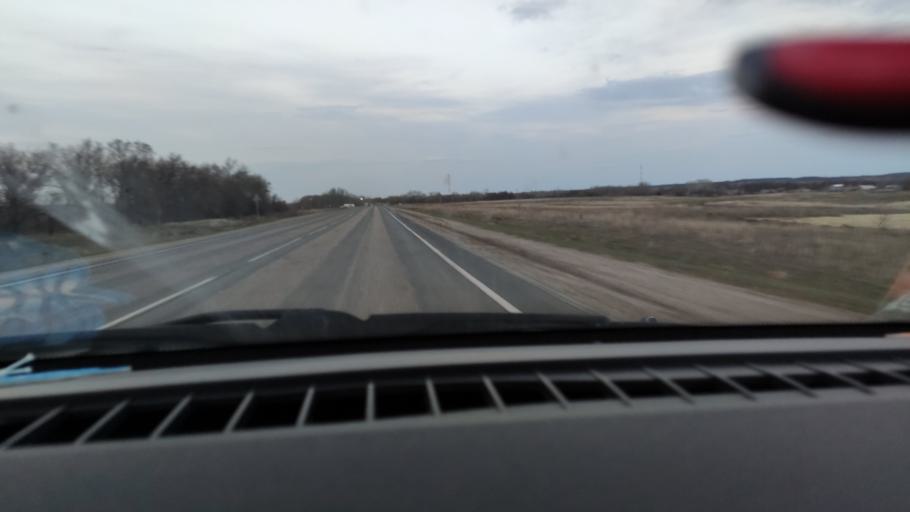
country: RU
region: Saratov
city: Sinodskoye
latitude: 51.9734
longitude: 46.6457
